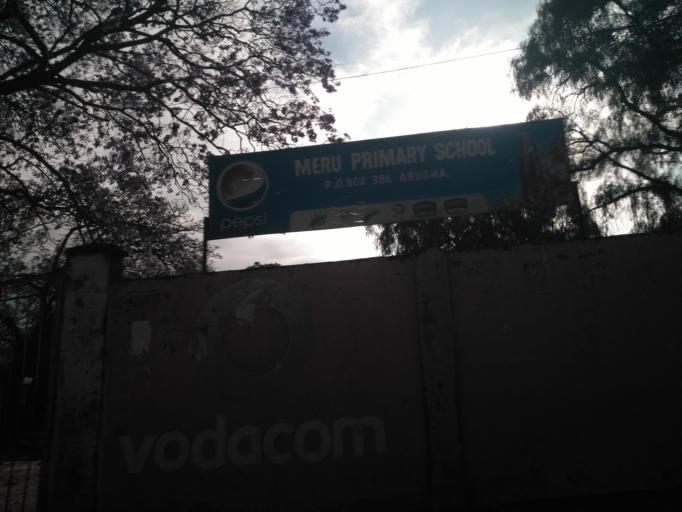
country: TZ
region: Arusha
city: Arusha
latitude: -3.3702
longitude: 36.6892
